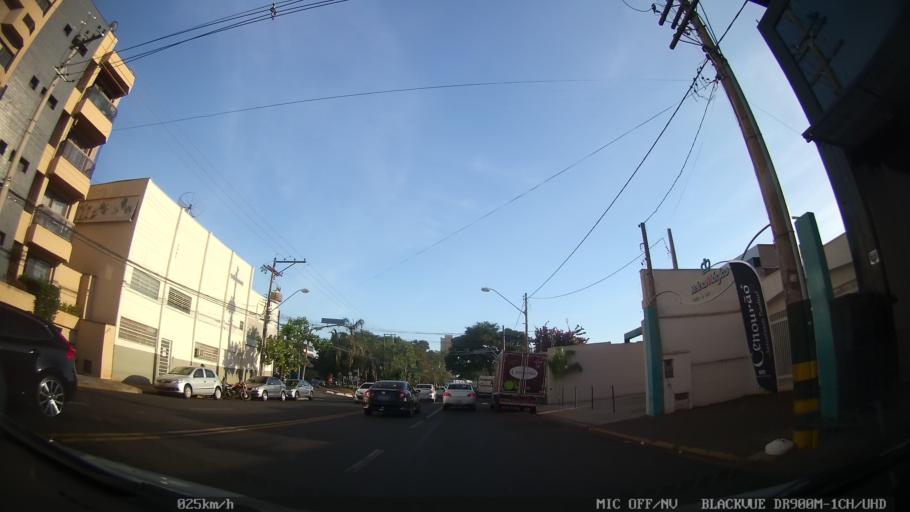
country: BR
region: Sao Paulo
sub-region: Ribeirao Preto
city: Ribeirao Preto
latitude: -21.1994
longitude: -47.7995
